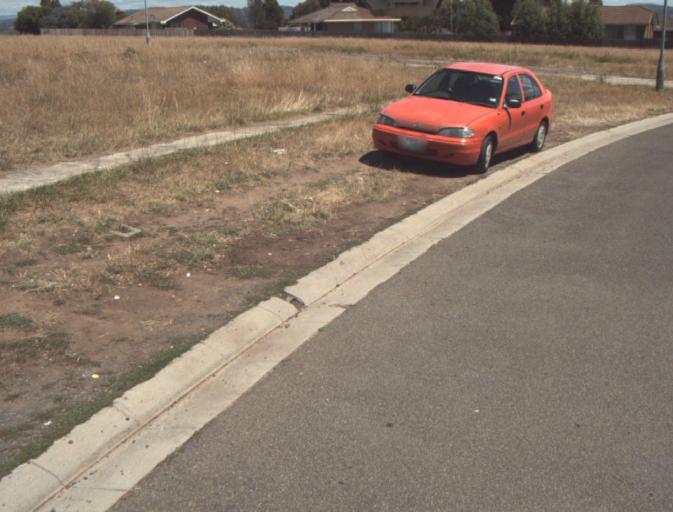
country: AU
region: Tasmania
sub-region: Launceston
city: Mayfield
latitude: -41.3757
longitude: 147.1405
